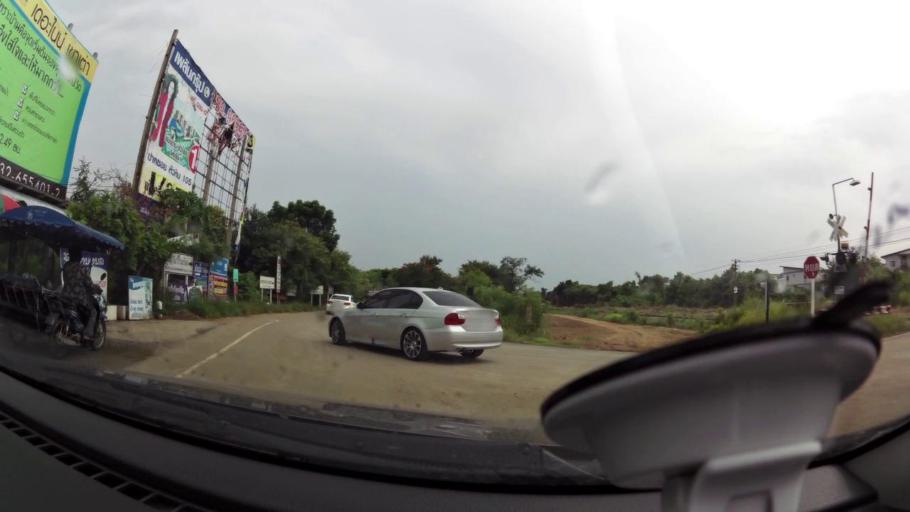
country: TH
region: Prachuap Khiri Khan
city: Pran Buri
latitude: 12.4471
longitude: 99.9635
